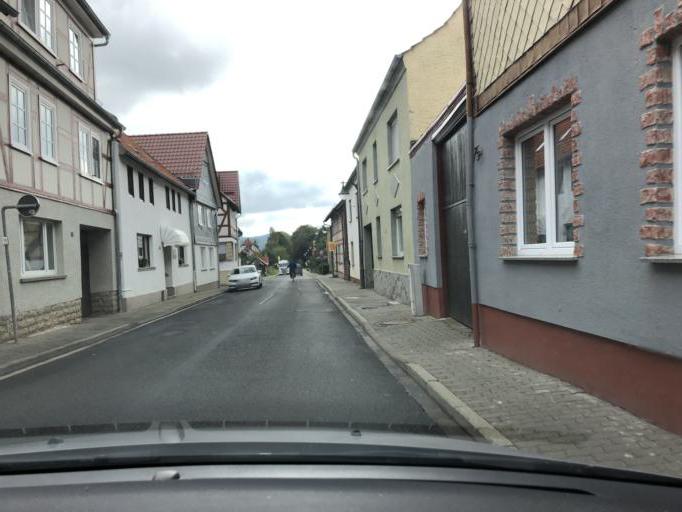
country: DE
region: Thuringia
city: Grossbartloff
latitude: 51.2487
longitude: 10.2100
